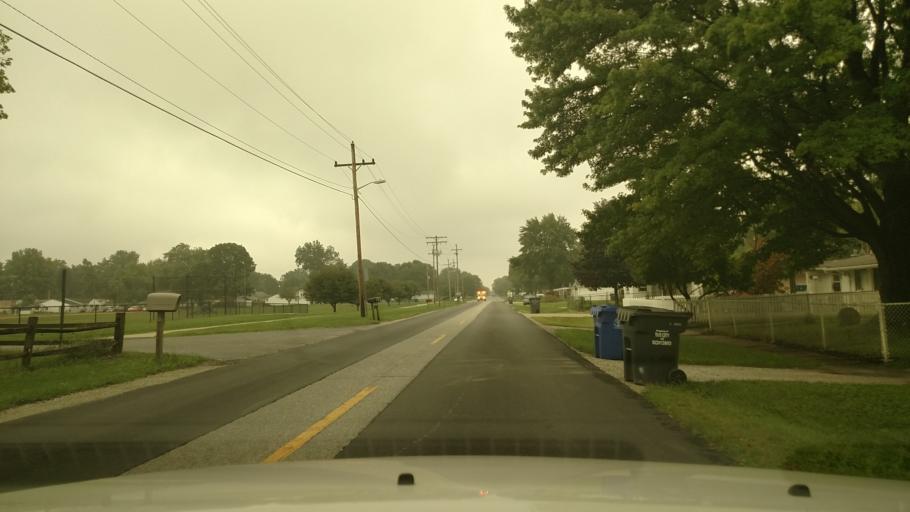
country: US
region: Indiana
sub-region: Howard County
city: Kokomo
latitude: 40.5147
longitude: -86.1270
